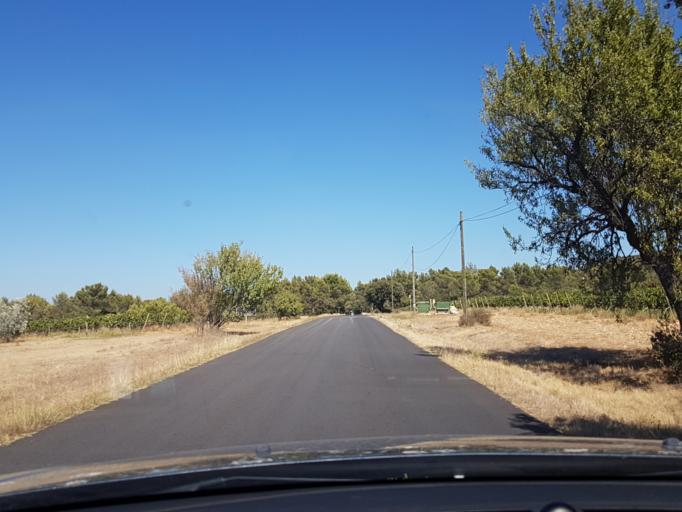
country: FR
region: Provence-Alpes-Cote d'Azur
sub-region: Departement des Bouches-du-Rhone
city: Orgon
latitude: 43.7731
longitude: 4.9957
